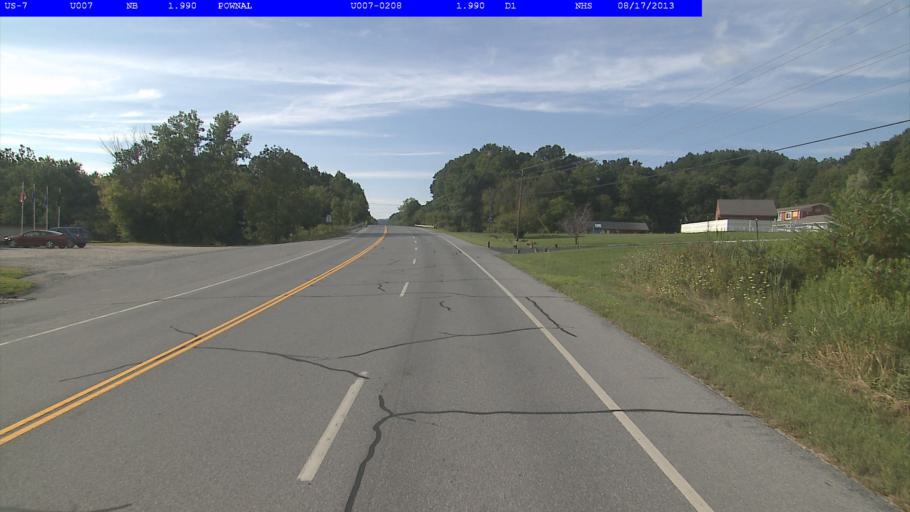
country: US
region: Massachusetts
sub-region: Berkshire County
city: Williamstown
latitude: 42.7652
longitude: -73.2326
